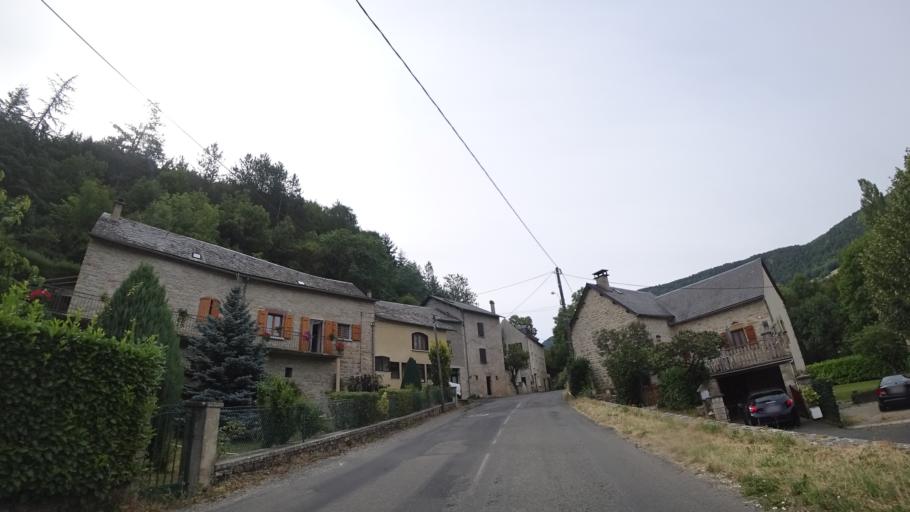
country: FR
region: Languedoc-Roussillon
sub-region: Departement de la Lozere
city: La Canourgue
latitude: 44.4266
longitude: 3.2229
